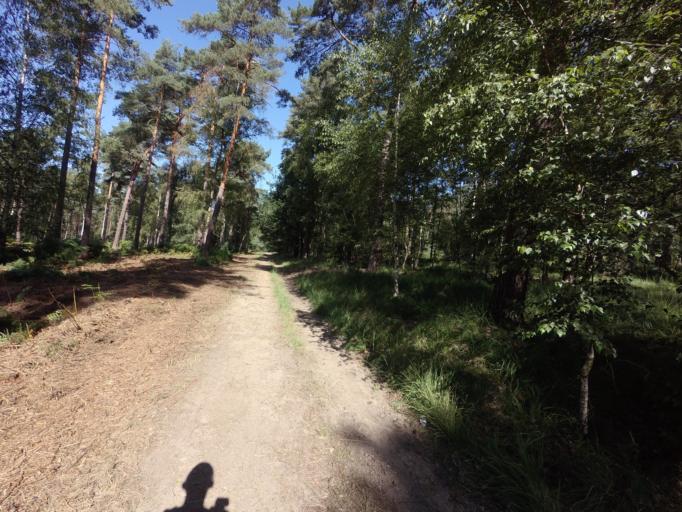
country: DE
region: North Rhine-Westphalia
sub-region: Regierungsbezirk Koln
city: Wassenberg
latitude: 51.1520
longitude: 6.1370
